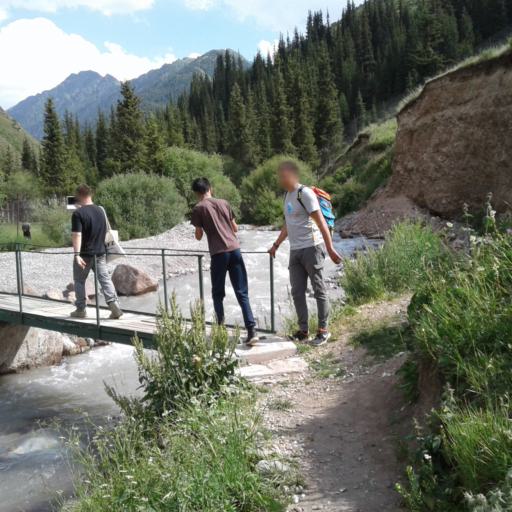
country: KG
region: Naryn
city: Naryn
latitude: 41.4568
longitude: 76.4530
